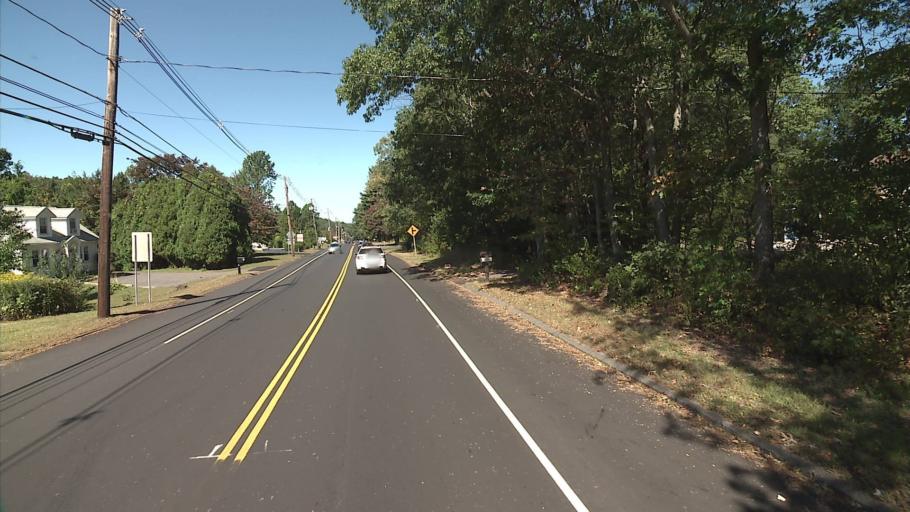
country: US
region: Connecticut
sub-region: New Haven County
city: Prospect
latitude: 41.5155
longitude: -72.9867
